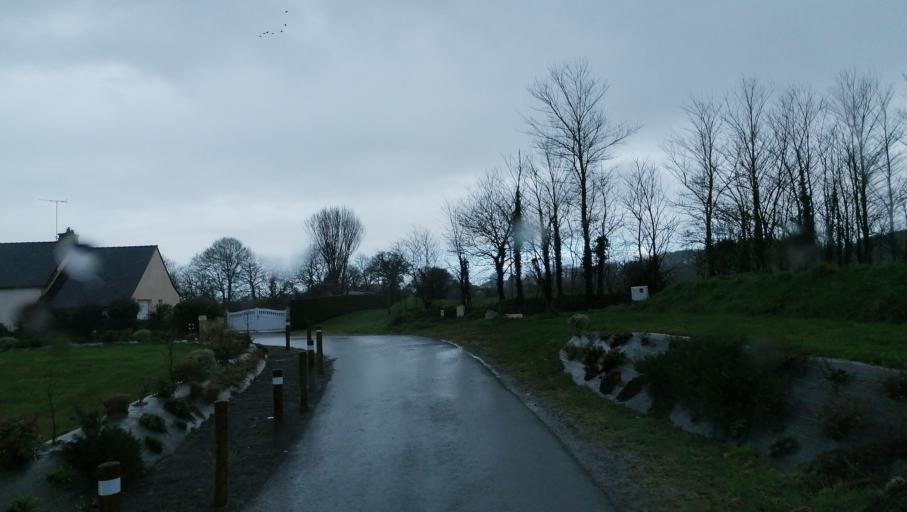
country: FR
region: Brittany
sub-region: Departement des Cotes-d'Armor
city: Plouagat
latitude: 48.4847
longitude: -2.9623
